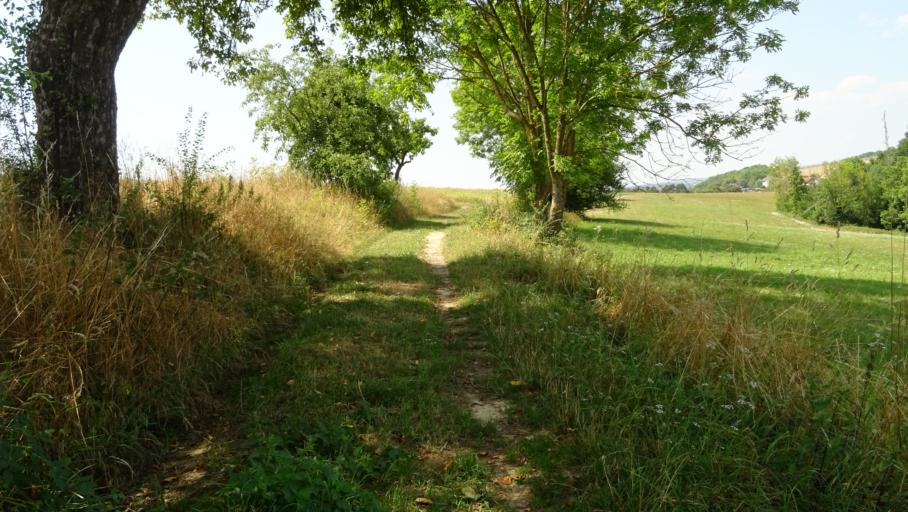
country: DE
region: Baden-Wuerttemberg
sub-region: Karlsruhe Region
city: Mosbach
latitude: 49.3539
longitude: 9.1236
